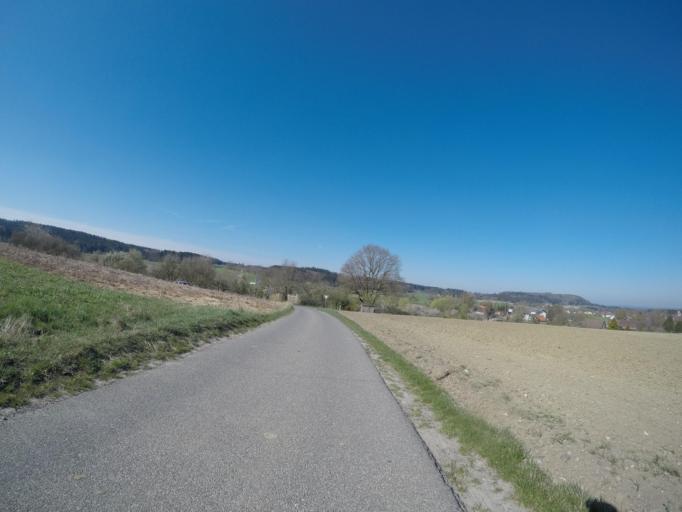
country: DE
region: Baden-Wuerttemberg
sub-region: Tuebingen Region
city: Fleischwangen
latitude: 47.8747
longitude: 9.4892
